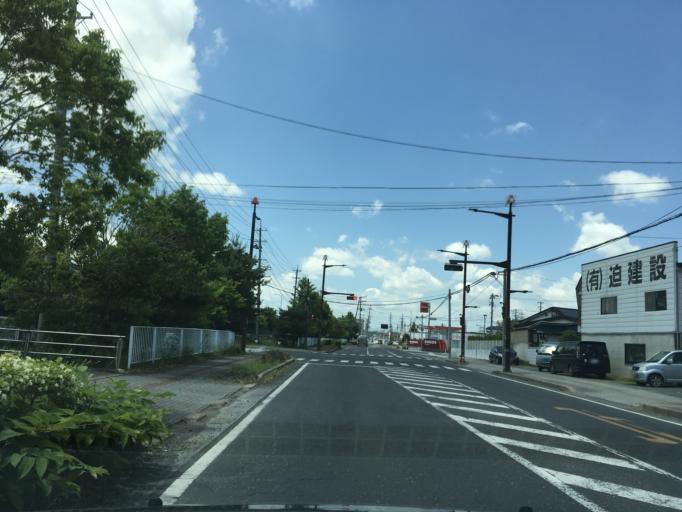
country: JP
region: Miyagi
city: Wakuya
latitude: 38.6823
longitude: 141.2090
